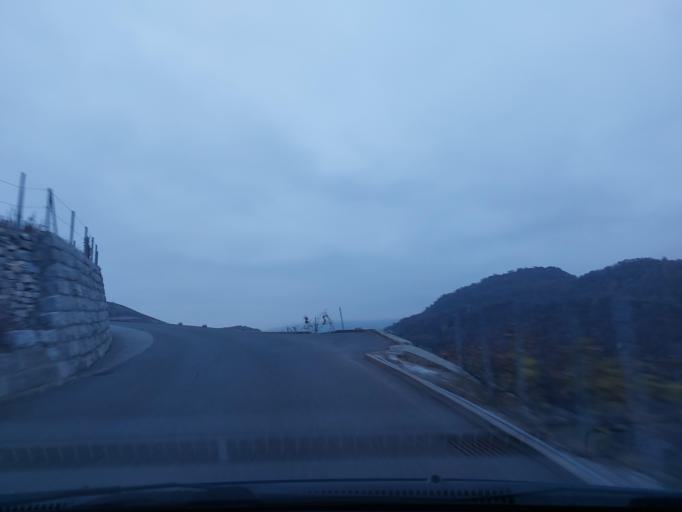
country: CH
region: Valais
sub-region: Conthey District
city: Conthey
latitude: 46.2357
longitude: 7.3207
